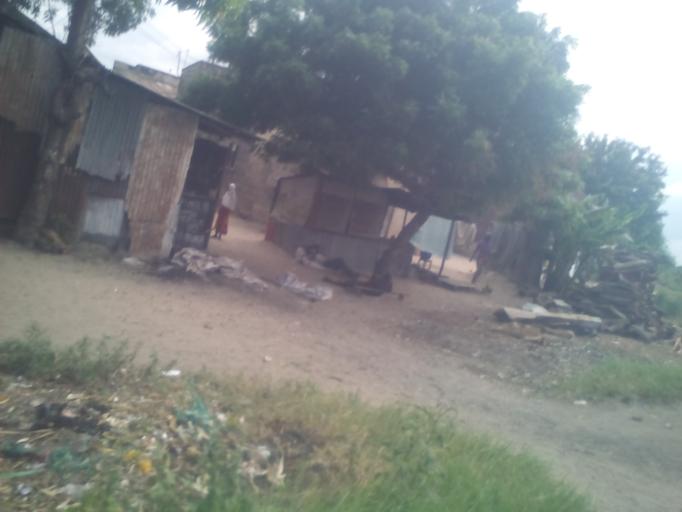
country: TZ
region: Dar es Salaam
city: Dar es Salaam
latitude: -6.8620
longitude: 39.2453
